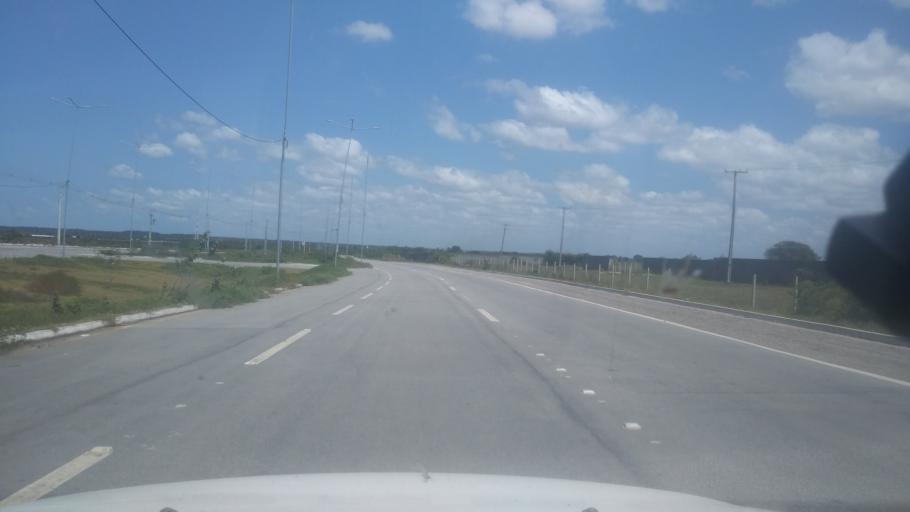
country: BR
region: Rio Grande do Norte
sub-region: Macaiba
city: Macaiba
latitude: -5.8547
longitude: -35.3790
